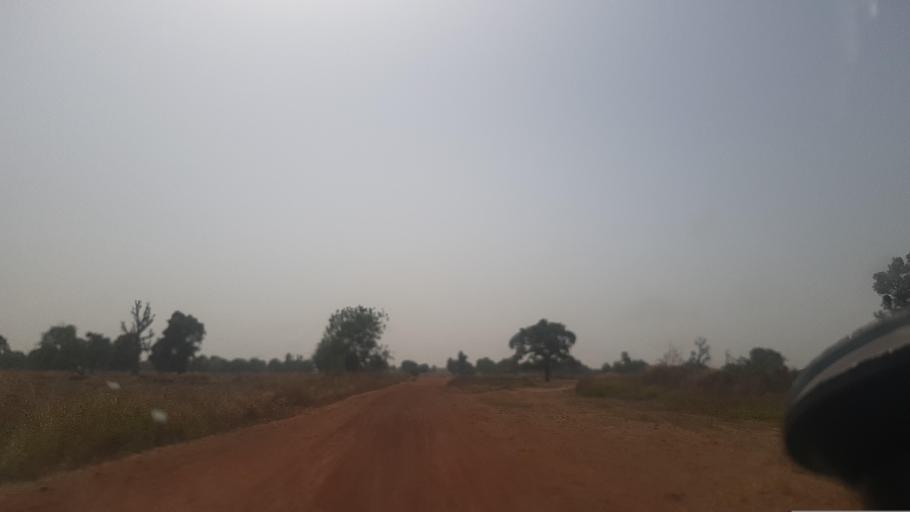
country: ML
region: Segou
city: Baroueli
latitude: 13.0087
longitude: -6.4213
